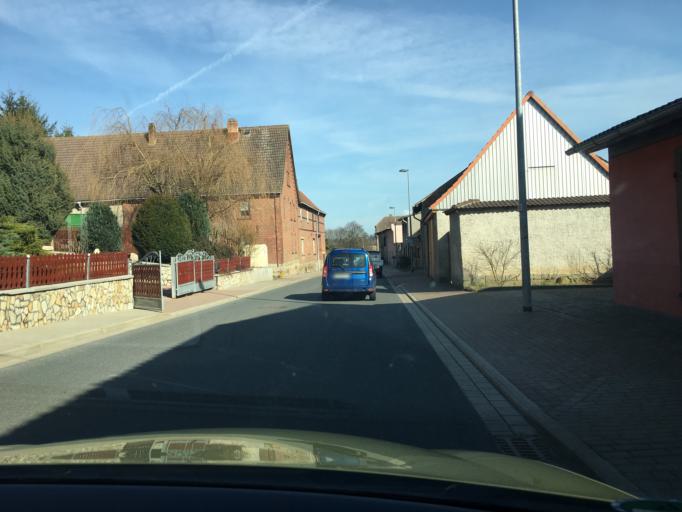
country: DE
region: Thuringia
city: Rastenberg
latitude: 51.2006
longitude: 11.4214
